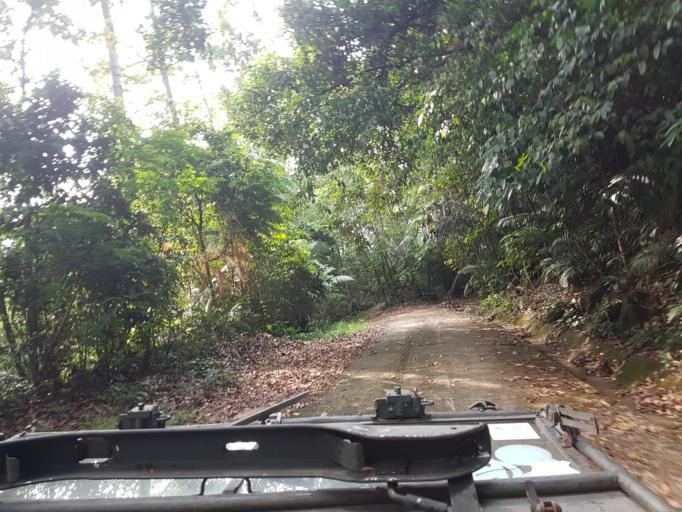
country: TH
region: Pattani
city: Khok Pho
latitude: 6.6575
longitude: 101.0990
